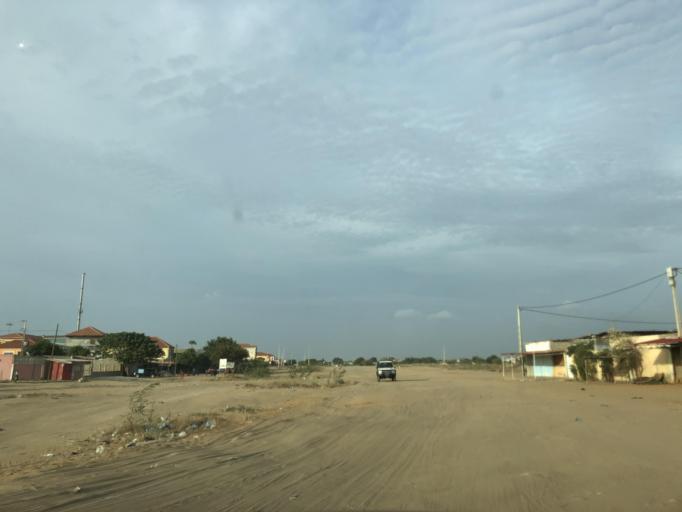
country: AO
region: Luanda
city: Luanda
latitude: -8.9142
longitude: 13.3128
